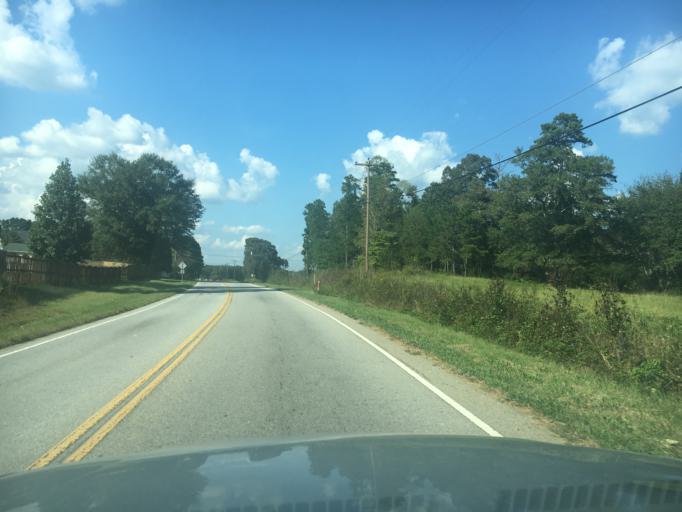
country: US
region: South Carolina
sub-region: Greenville County
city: Fountain Inn
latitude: 34.6467
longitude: -82.2574
